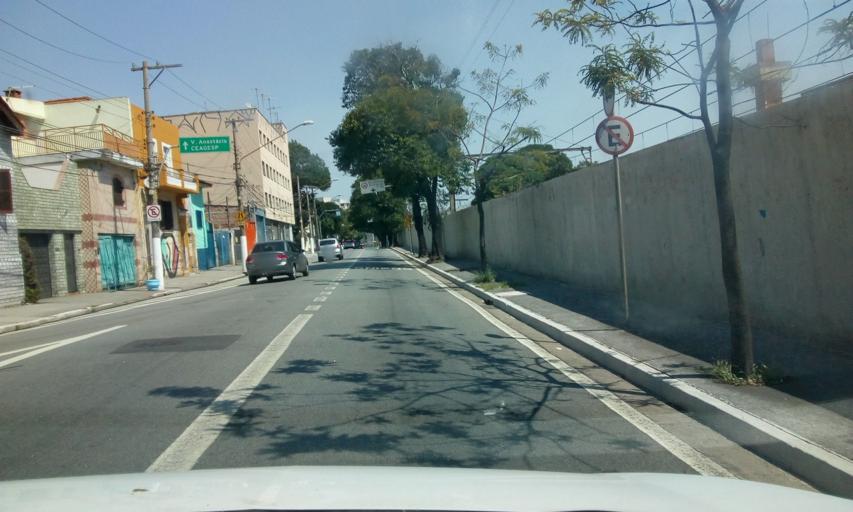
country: BR
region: Sao Paulo
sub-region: Sao Paulo
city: Sao Paulo
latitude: -23.5177
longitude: -46.7074
